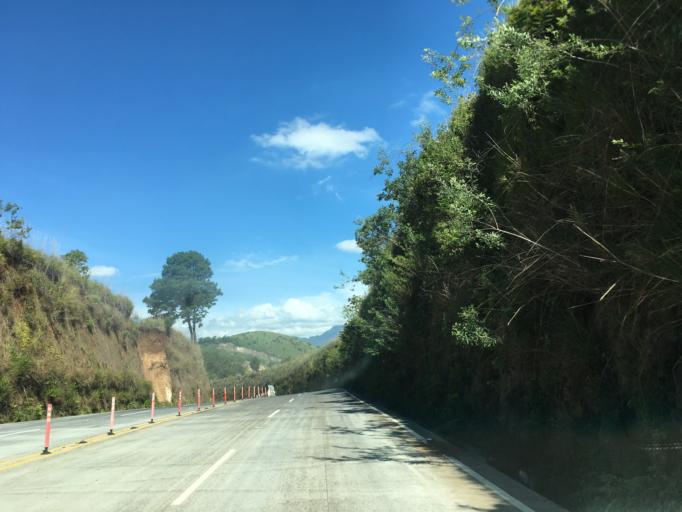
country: GT
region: Guatemala
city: Petapa
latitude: 14.4873
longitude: -90.5498
